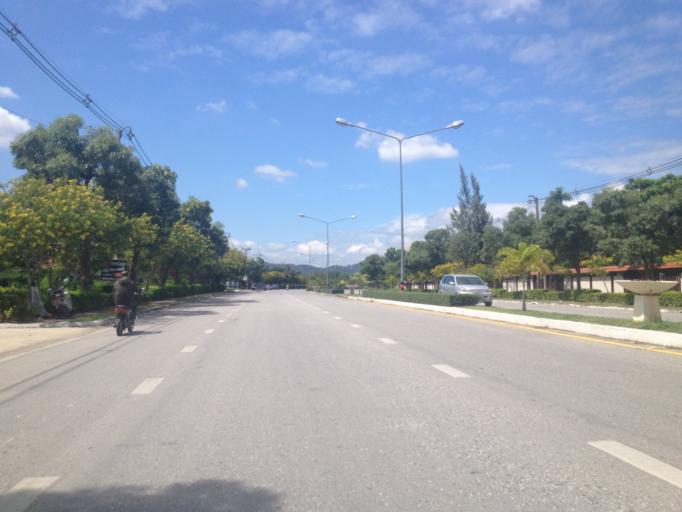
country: TH
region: Chiang Mai
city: Hang Dong
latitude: 18.7286
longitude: 98.9448
